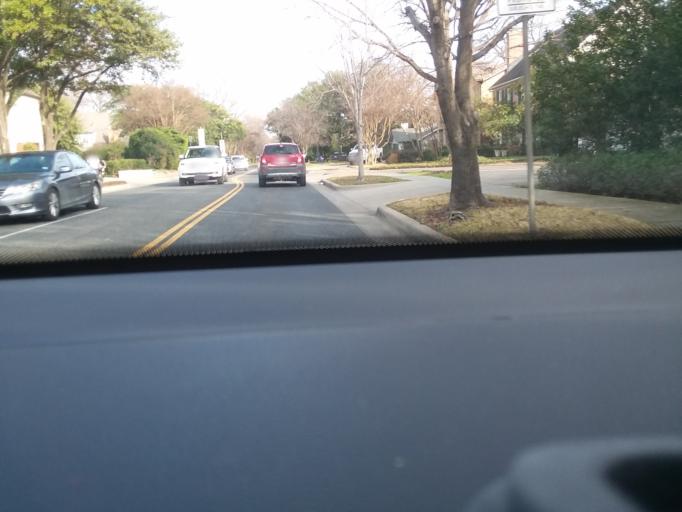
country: US
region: Texas
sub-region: Dallas County
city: Highland Park
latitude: 32.8365
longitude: -96.7907
